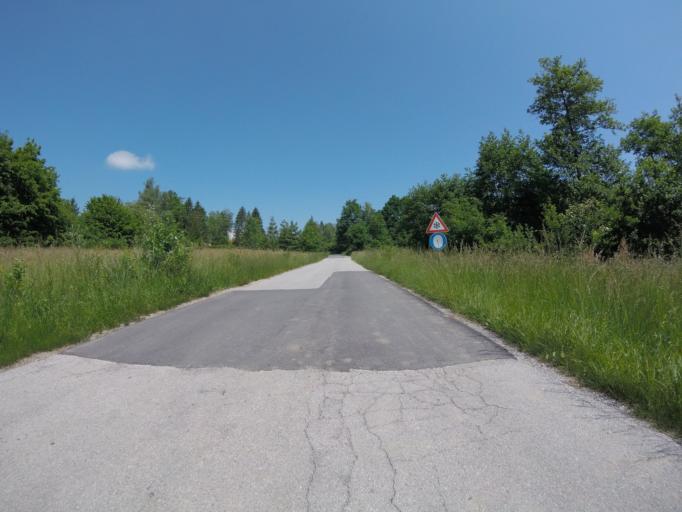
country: HR
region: Grad Zagreb
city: Strmec
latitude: 45.5689
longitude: 15.9469
